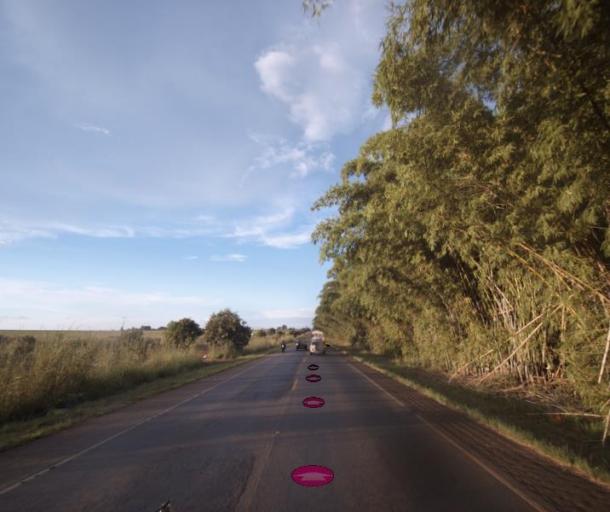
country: BR
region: Goias
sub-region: Anapolis
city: Anapolis
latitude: -16.2186
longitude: -48.9212
